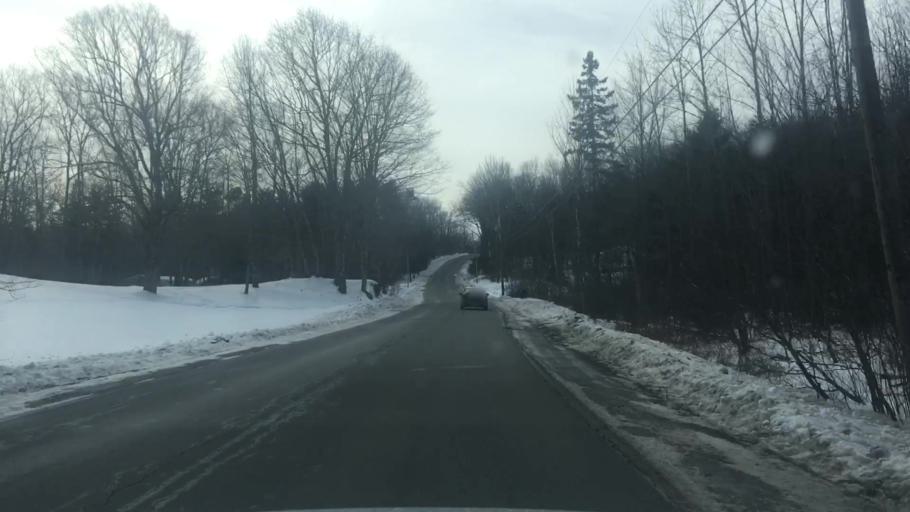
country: US
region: Maine
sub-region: Hancock County
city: Orland
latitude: 44.6140
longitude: -68.7109
